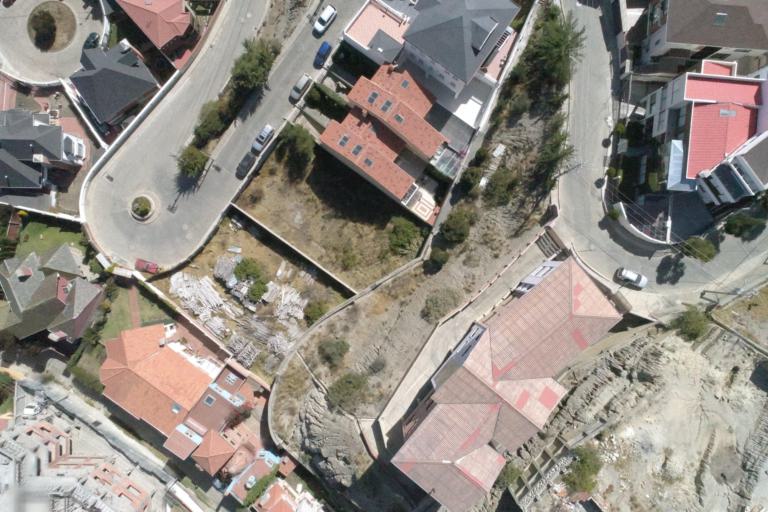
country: BO
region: La Paz
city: La Paz
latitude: -16.5344
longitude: -68.0706
